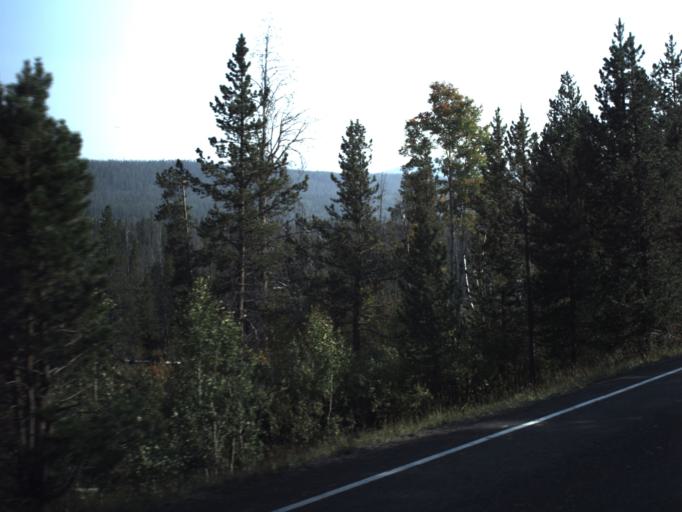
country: US
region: Wyoming
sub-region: Uinta County
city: Evanston
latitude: 40.8352
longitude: -110.8503
